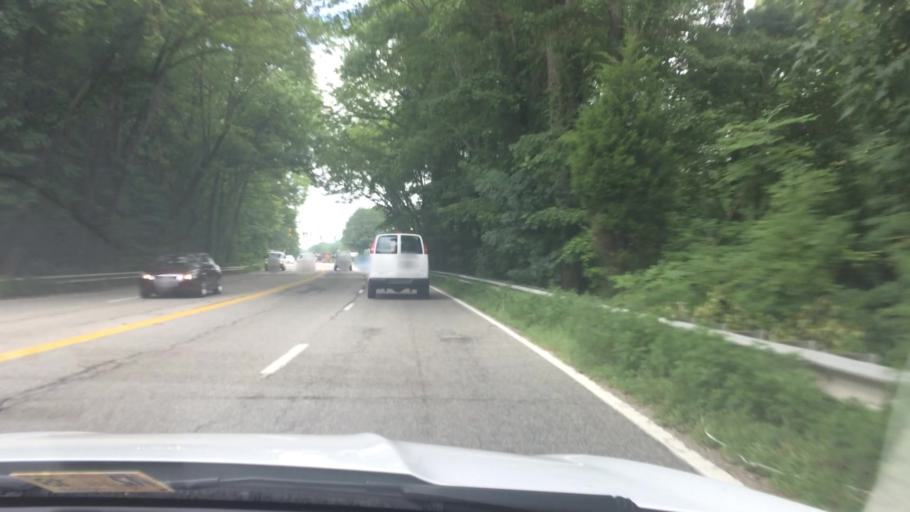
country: US
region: Virginia
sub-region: York County
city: Yorktown
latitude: 37.2123
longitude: -76.5811
